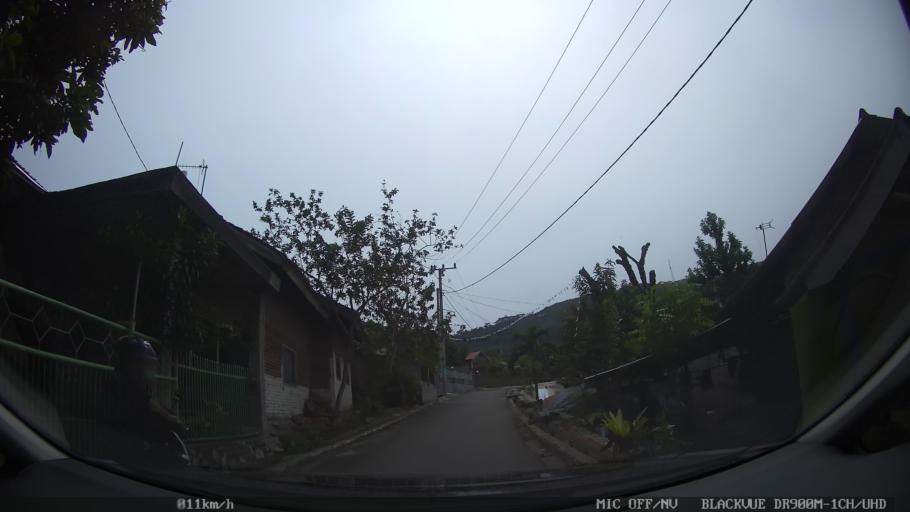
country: ID
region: Lampung
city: Bandarlampung
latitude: -5.4305
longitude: 105.2971
